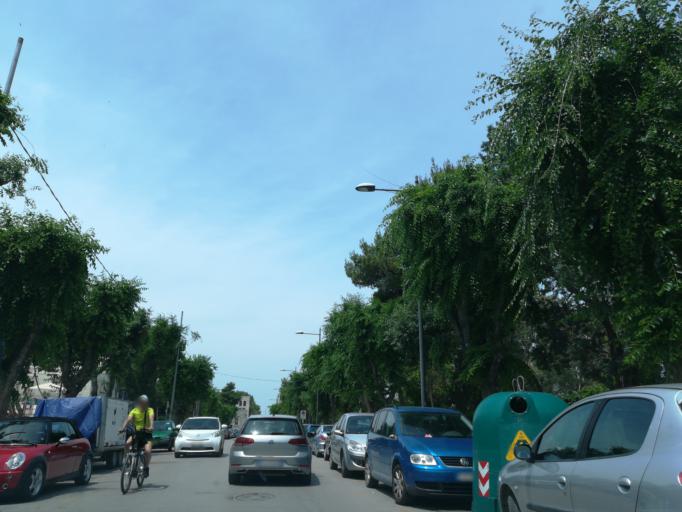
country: IT
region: Apulia
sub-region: Provincia di Barletta - Andria - Trani
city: Barletta
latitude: 41.3215
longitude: 16.2865
